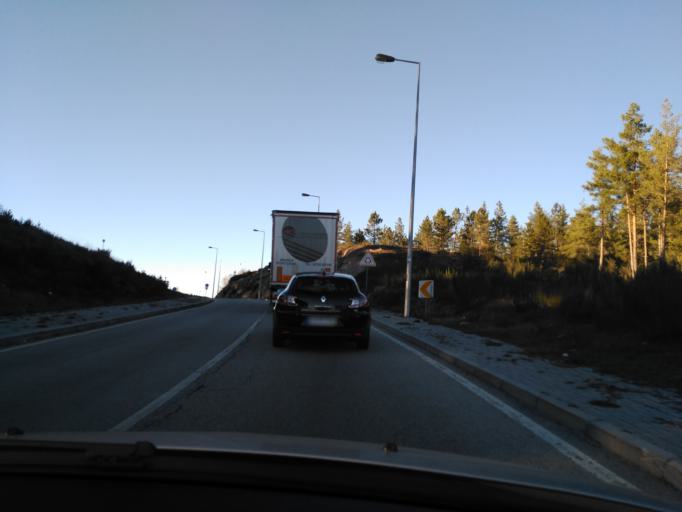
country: PT
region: Vila Real
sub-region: Montalegre
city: Montalegre
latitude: 41.8125
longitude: -7.7891
